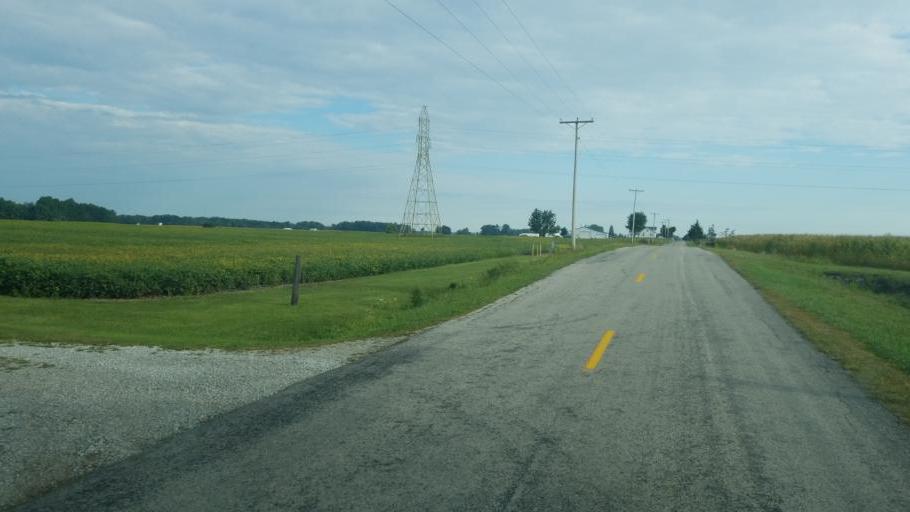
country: US
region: Ohio
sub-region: Crawford County
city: Galion
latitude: 40.6808
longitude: -82.9098
